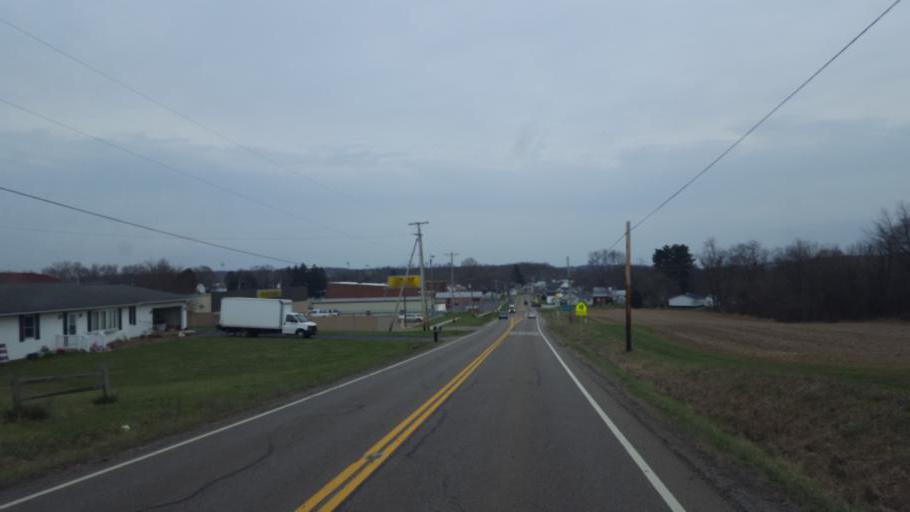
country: US
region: Ohio
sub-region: Knox County
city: Gambier
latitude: 40.4087
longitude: -82.3341
